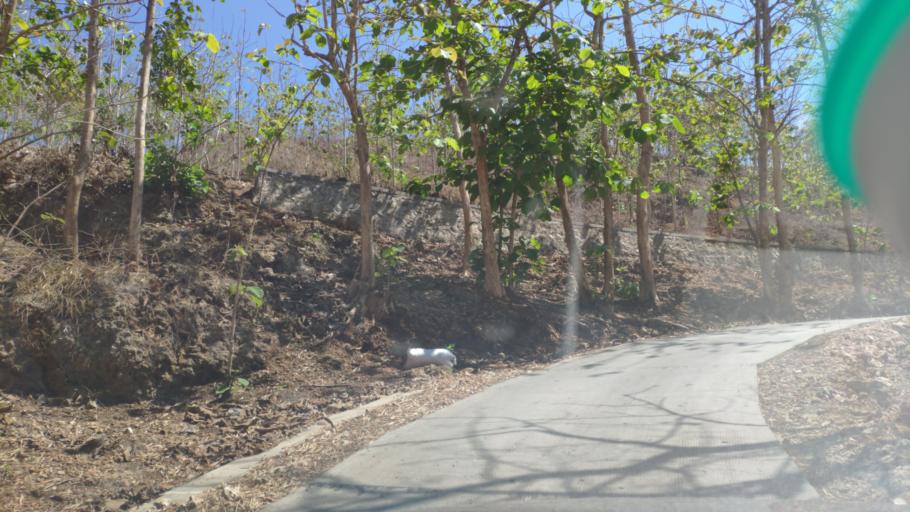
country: ID
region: Central Java
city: Jurangjero
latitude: -6.9002
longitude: 111.5076
